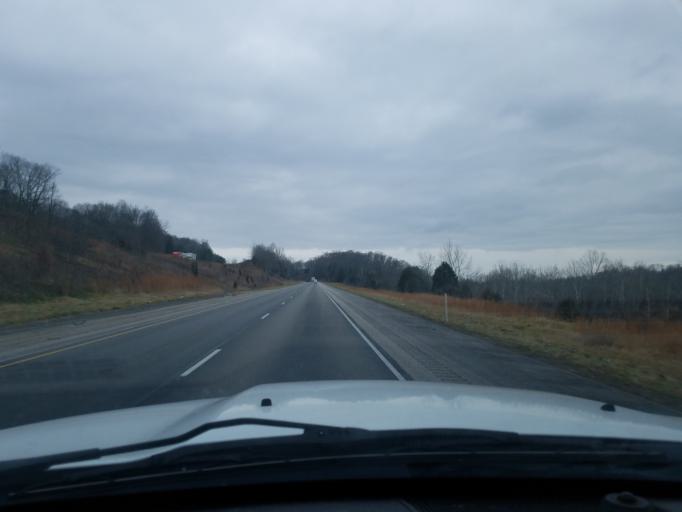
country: US
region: Indiana
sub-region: Crawford County
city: English
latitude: 38.2393
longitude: -86.5334
